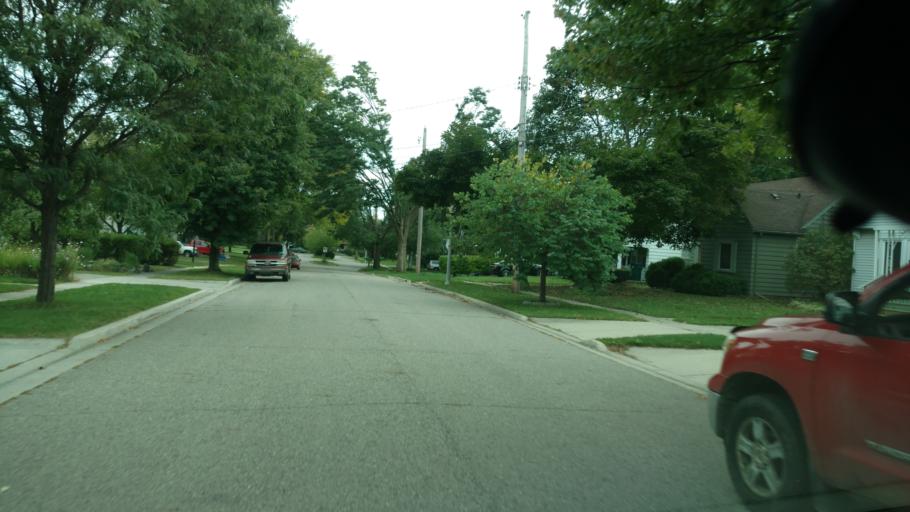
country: US
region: Michigan
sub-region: Ingham County
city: East Lansing
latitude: 42.7396
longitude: -84.5138
